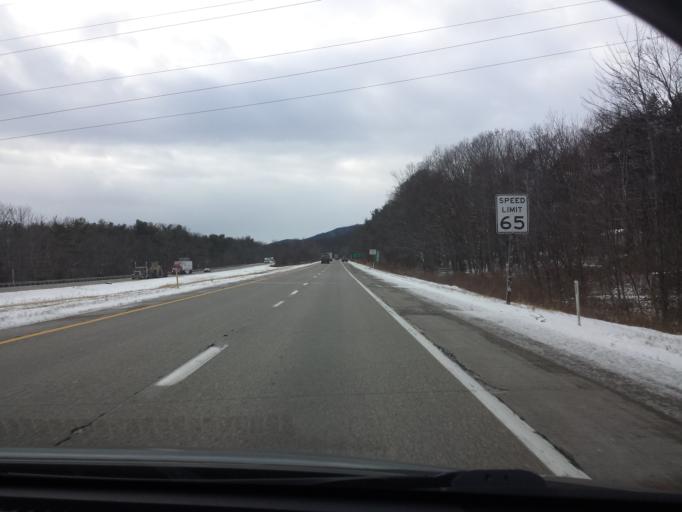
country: US
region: Pennsylvania
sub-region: Luzerne County
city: Conyngham
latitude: 41.0257
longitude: -76.0902
